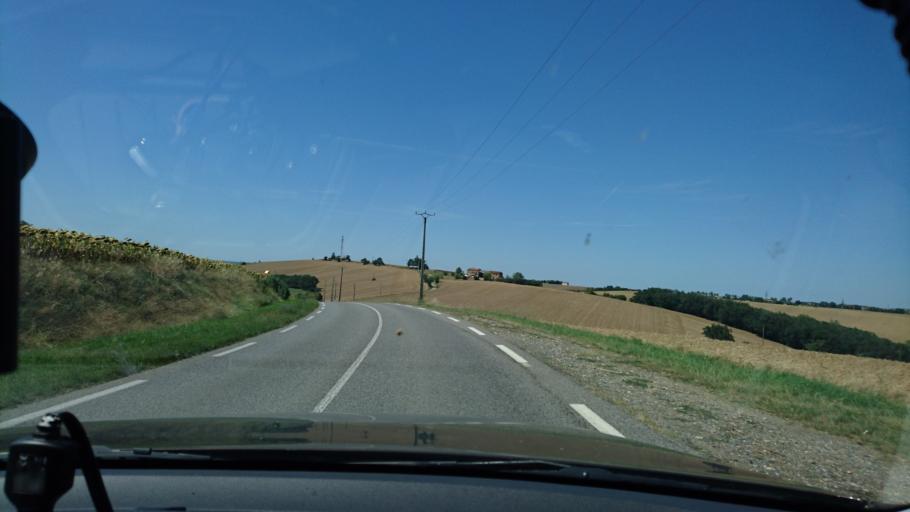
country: FR
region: Midi-Pyrenees
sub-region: Departement de la Haute-Garonne
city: Saint-Sulpice-sur-Leze
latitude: 43.3357
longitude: 1.2946
